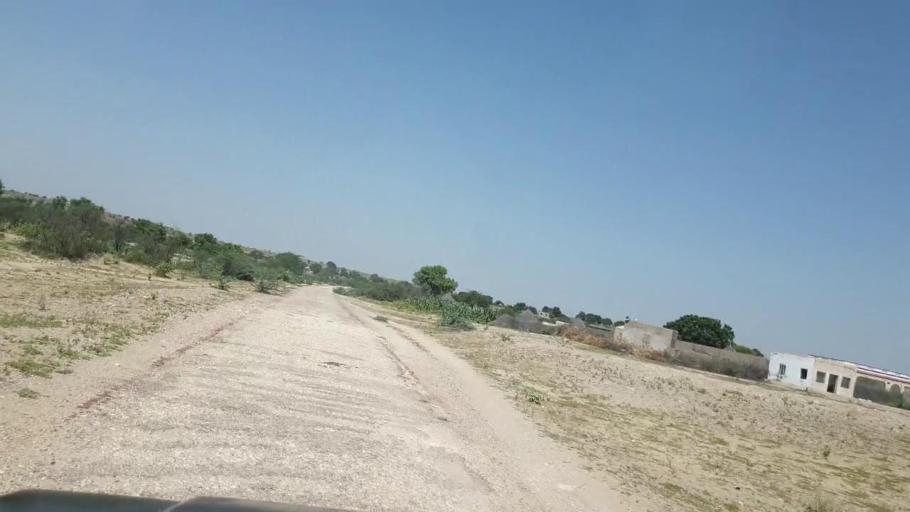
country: PK
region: Sindh
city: Chor
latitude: 25.3730
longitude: 70.3171
